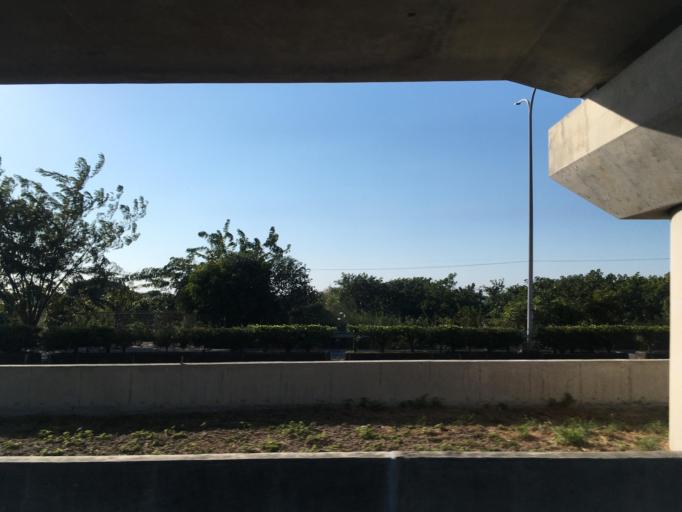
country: TW
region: Taiwan
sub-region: Chiayi
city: Taibao
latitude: 23.4424
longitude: 120.3231
